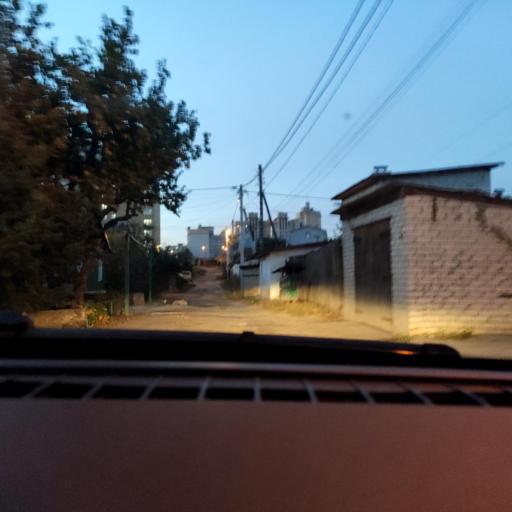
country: RU
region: Voronezj
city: Voronezh
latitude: 51.6789
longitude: 39.2465
